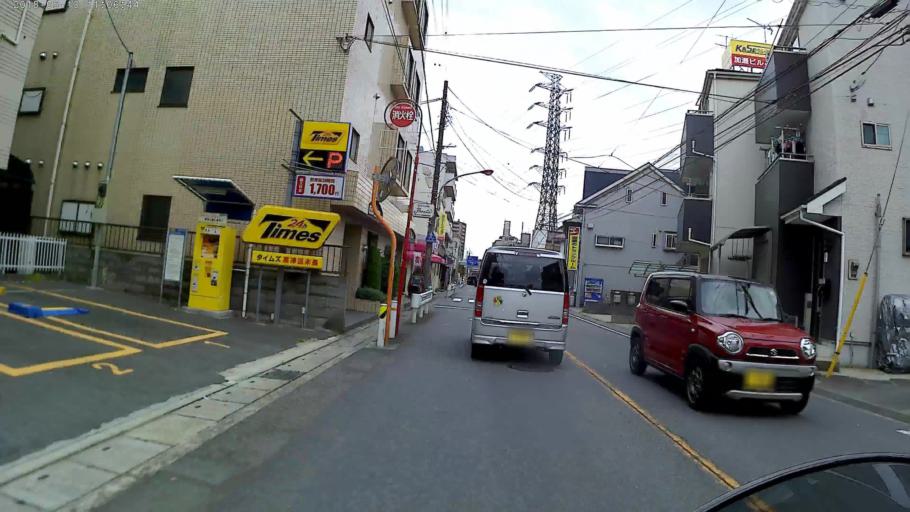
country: JP
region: Tokyo
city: Chofugaoka
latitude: 35.5894
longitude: 139.6171
